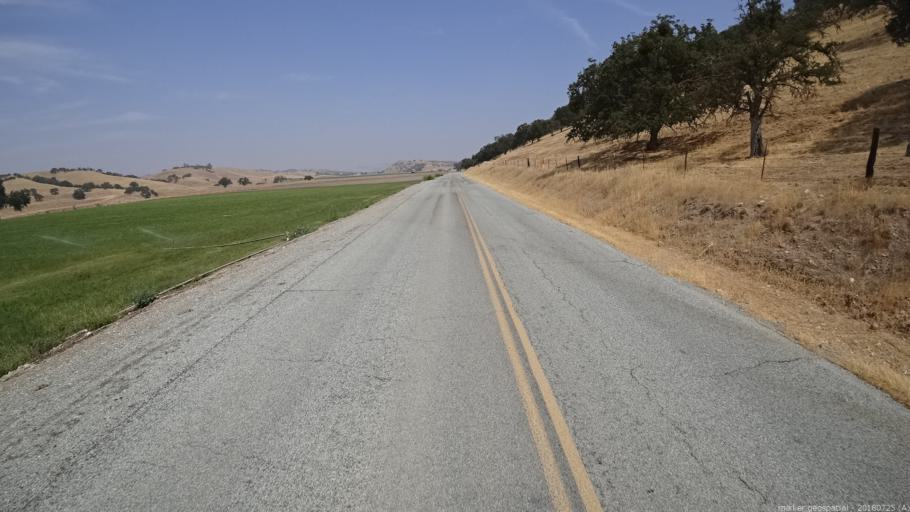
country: US
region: California
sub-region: San Luis Obispo County
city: San Miguel
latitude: 35.8141
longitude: -120.6655
